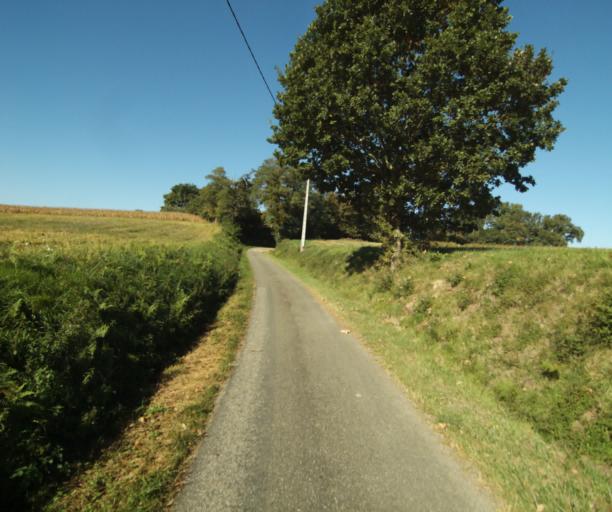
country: FR
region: Midi-Pyrenees
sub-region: Departement du Gers
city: Eauze
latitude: 43.8080
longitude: 0.1739
